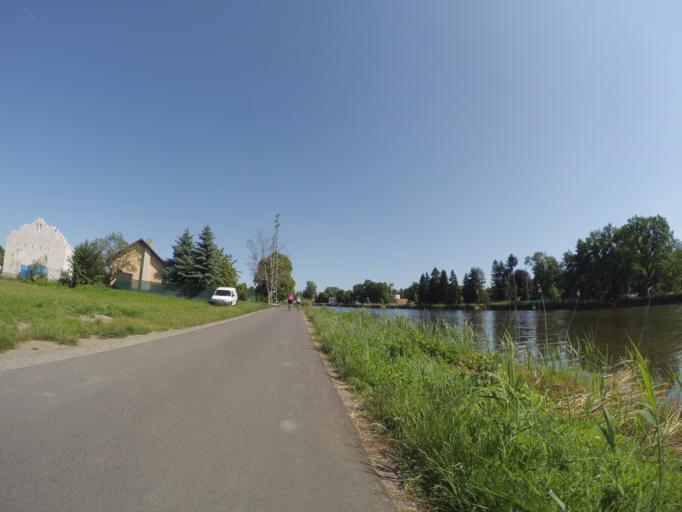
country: CZ
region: Central Bohemia
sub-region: Okres Nymburk
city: Nymburk
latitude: 50.1825
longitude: 15.0560
